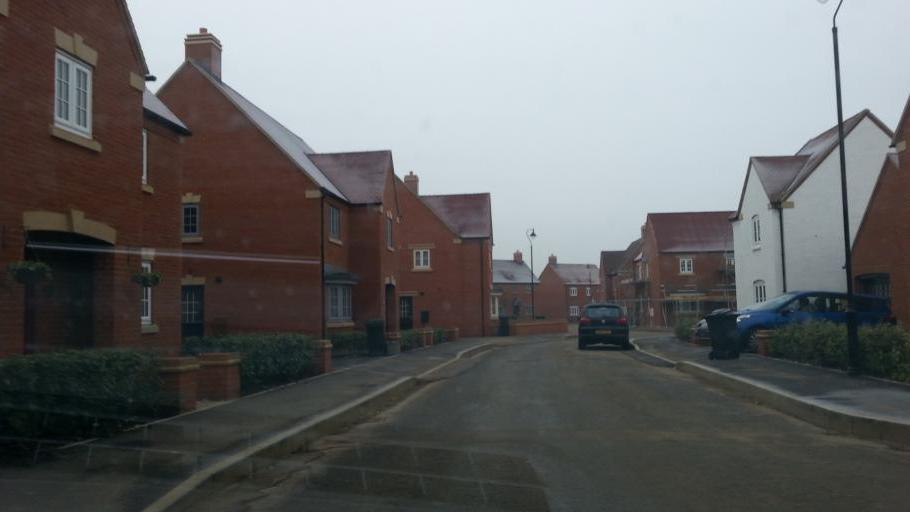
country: GB
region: England
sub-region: Northamptonshire
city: Brackley
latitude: 52.0453
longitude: -1.1515
